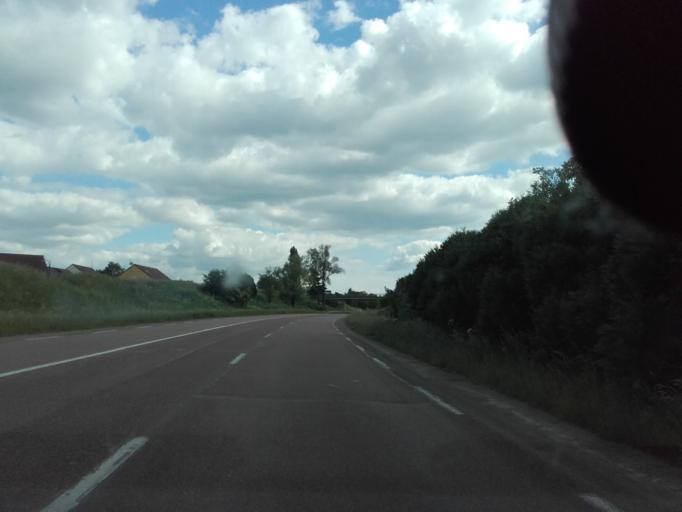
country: FR
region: Bourgogne
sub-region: Departement de Saone-et-Loire
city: Chagny
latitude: 46.9109
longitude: 4.7588
